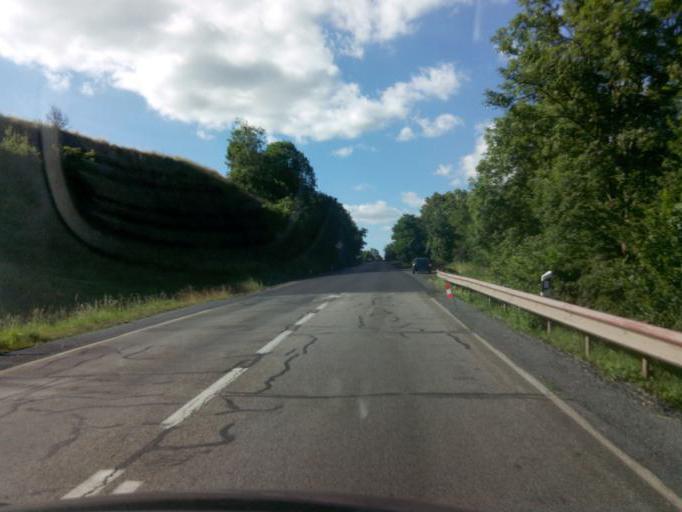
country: FR
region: Auvergne
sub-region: Departement de la Haute-Loire
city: Polignac
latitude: 45.0681
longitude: 3.8497
